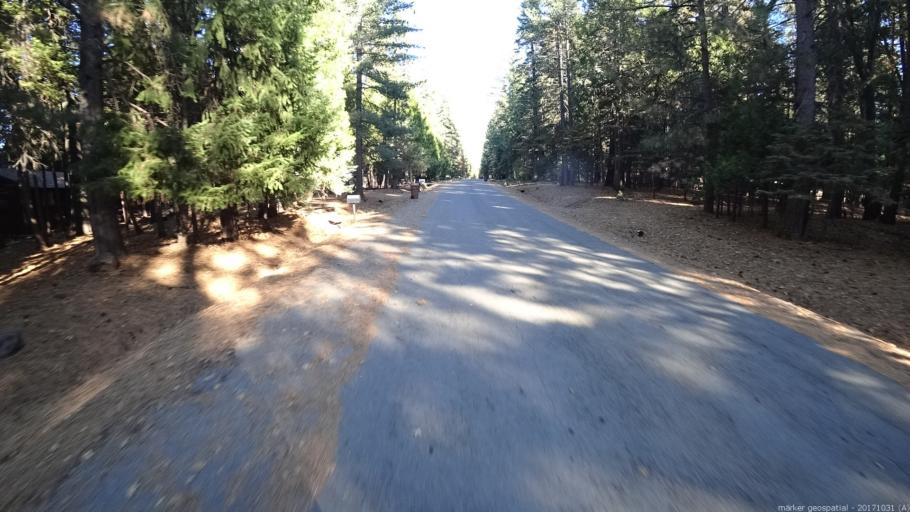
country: US
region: California
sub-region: Shasta County
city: Shingletown
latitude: 40.5030
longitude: -121.9104
